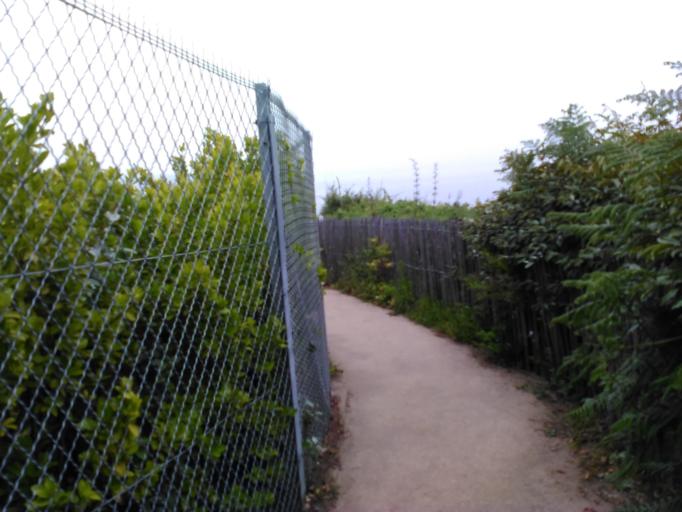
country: FR
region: Brittany
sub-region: Departement du Finistere
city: Fouesnant
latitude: 47.8558
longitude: -3.9759
